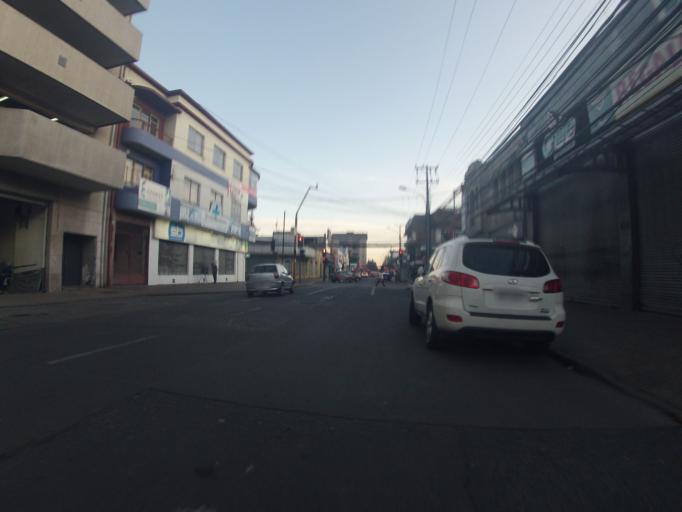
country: CL
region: Araucania
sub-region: Provincia de Cautin
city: Temuco
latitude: -38.7379
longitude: -72.5918
